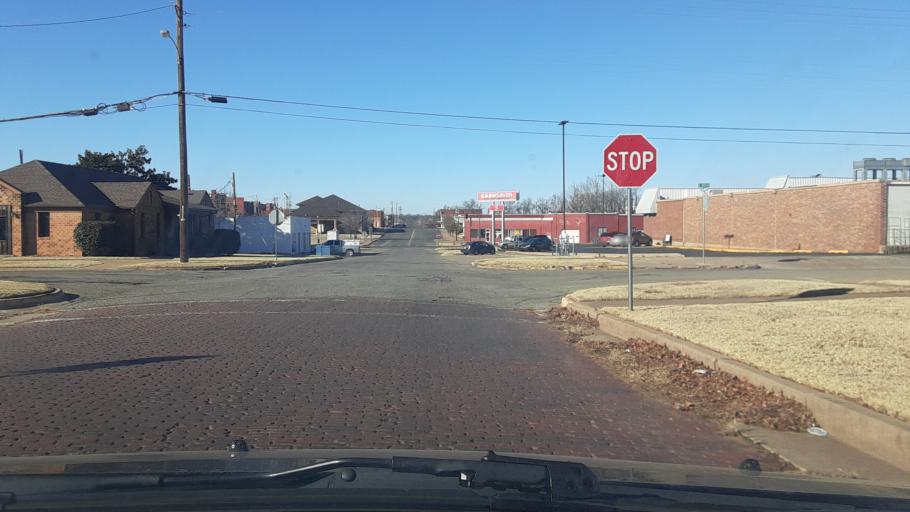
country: US
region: Oklahoma
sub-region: Logan County
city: Guthrie
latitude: 35.8791
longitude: -97.4225
